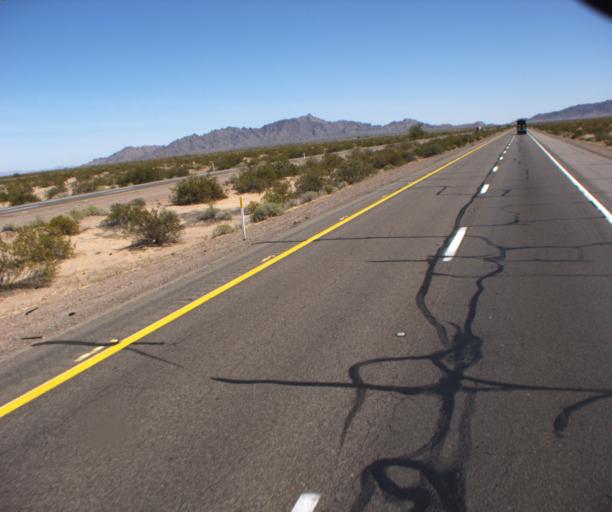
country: US
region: Arizona
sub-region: Yuma County
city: Wellton
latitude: 32.7086
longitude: -113.8533
